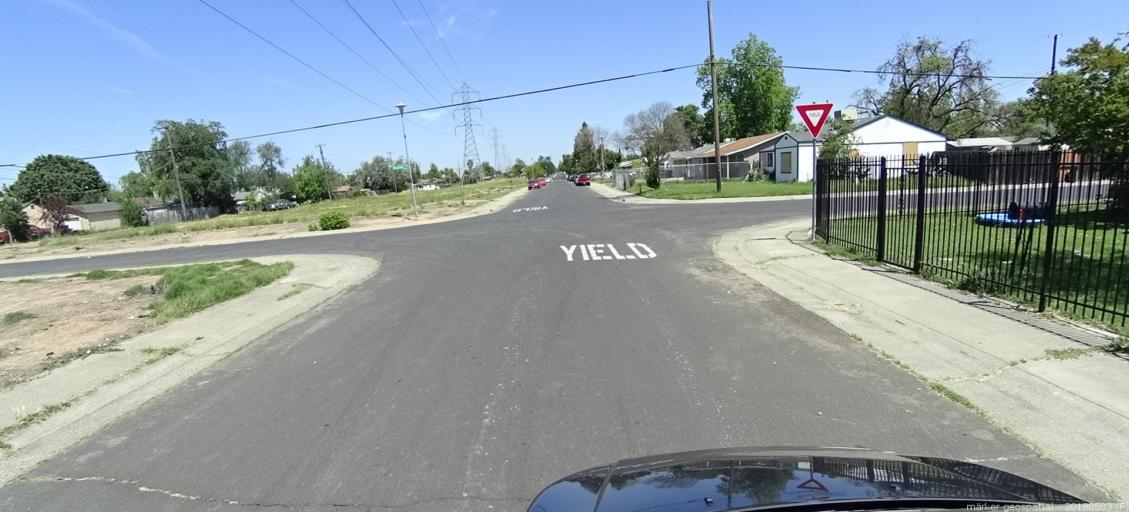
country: US
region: California
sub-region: Sacramento County
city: Arden-Arcade
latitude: 38.6343
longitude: -121.4222
